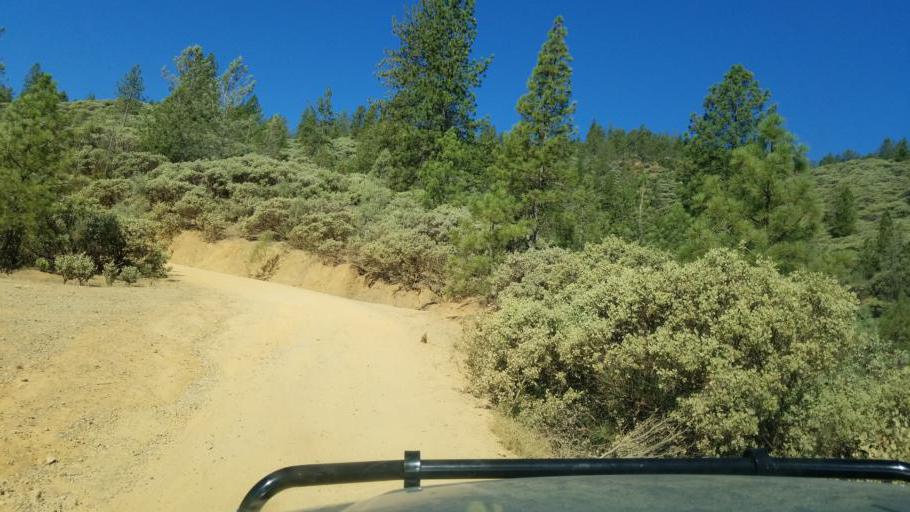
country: US
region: California
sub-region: Shasta County
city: Shasta
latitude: 40.6635
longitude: -122.4631
